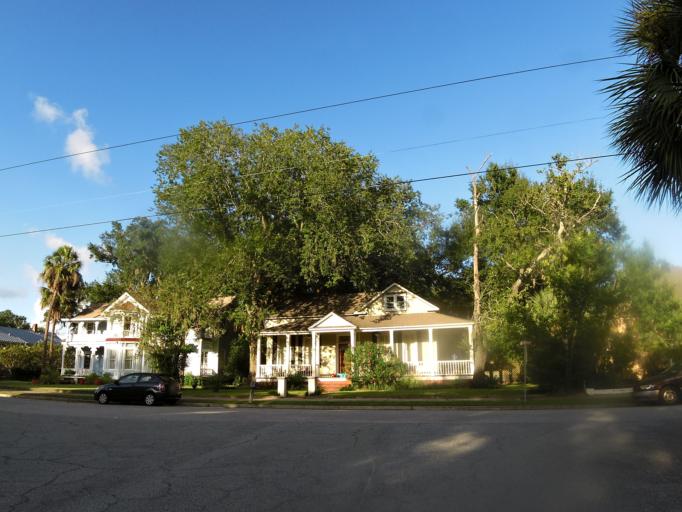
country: US
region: Georgia
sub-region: Glynn County
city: Brunswick
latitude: 31.1429
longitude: -81.4928
